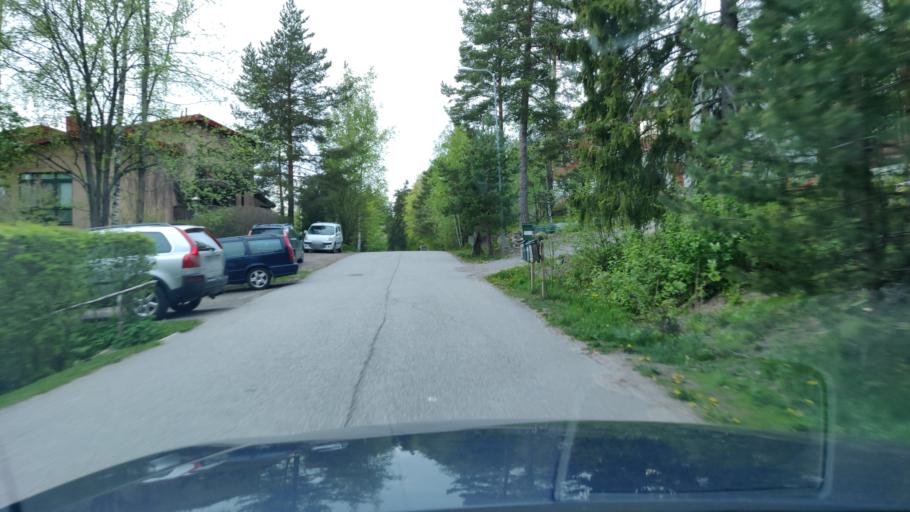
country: FI
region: Uusimaa
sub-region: Helsinki
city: Nurmijaervi
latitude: 60.3850
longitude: 24.7509
